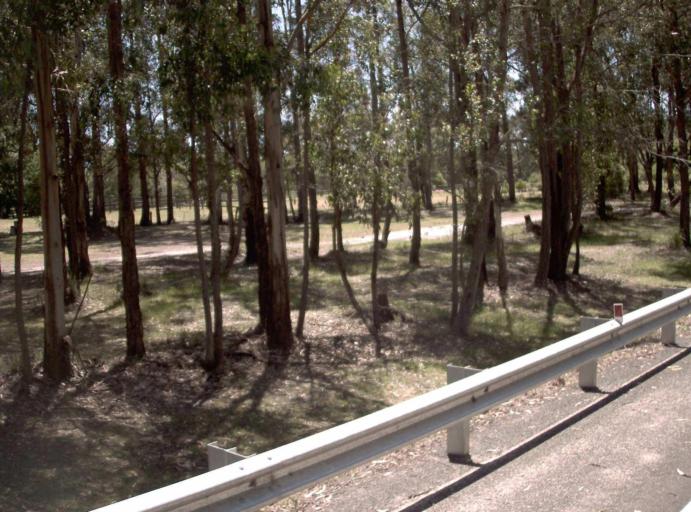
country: AU
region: Victoria
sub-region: East Gippsland
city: Lakes Entrance
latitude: -37.7752
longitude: 148.0512
